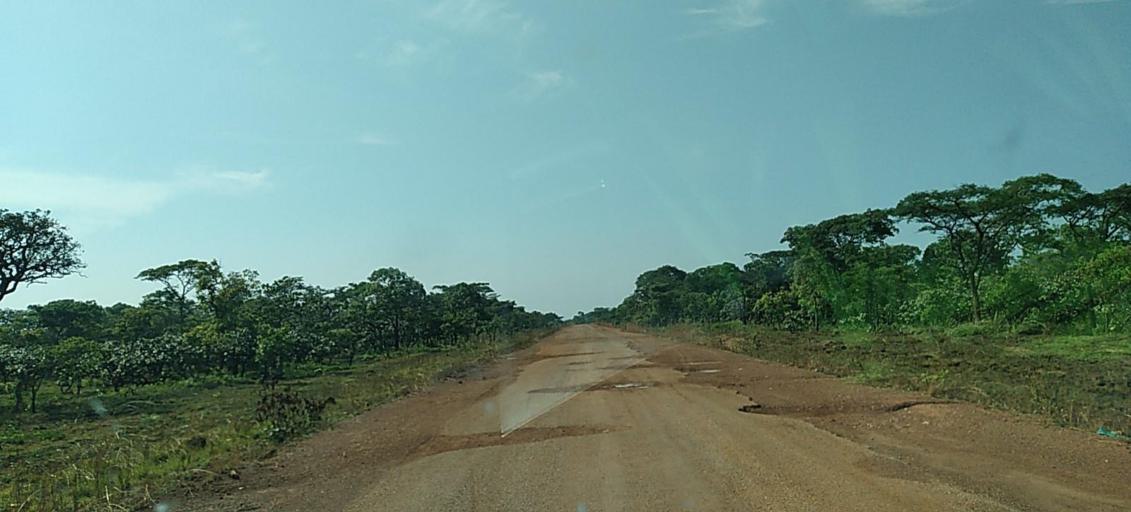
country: ZM
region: North-Western
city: Mwinilunga
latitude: -11.7960
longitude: 25.0731
